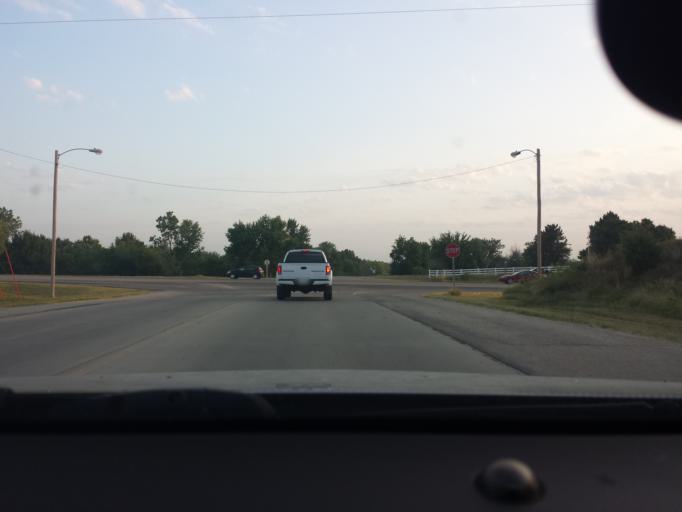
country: US
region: Kansas
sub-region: Pottawatomie County
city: Wamego
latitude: 39.2098
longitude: -96.3248
